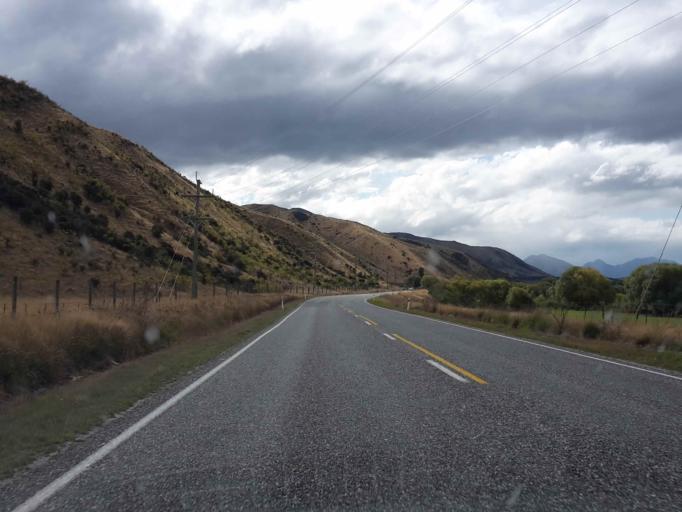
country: NZ
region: Otago
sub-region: Queenstown-Lakes District
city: Wanaka
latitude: -44.8044
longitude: 169.0693
